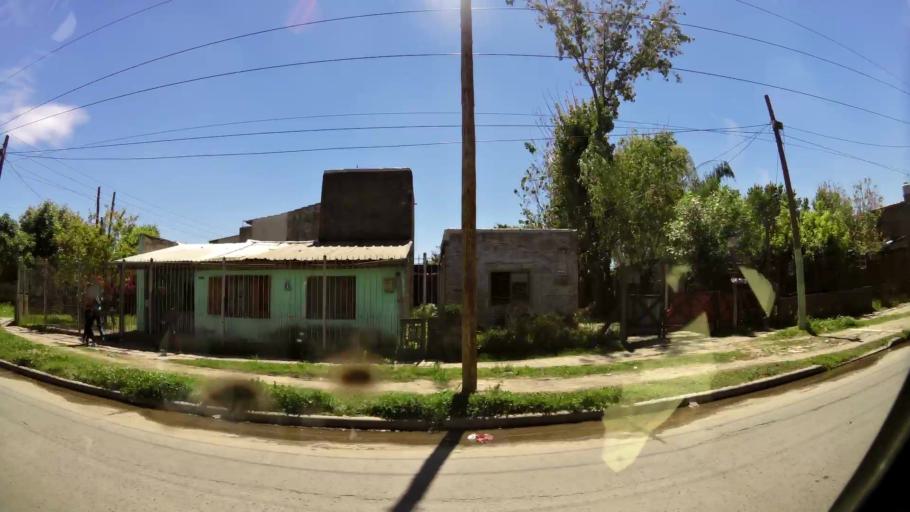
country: AR
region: Buenos Aires
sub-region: Partido de Quilmes
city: Quilmes
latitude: -34.7249
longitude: -58.3150
